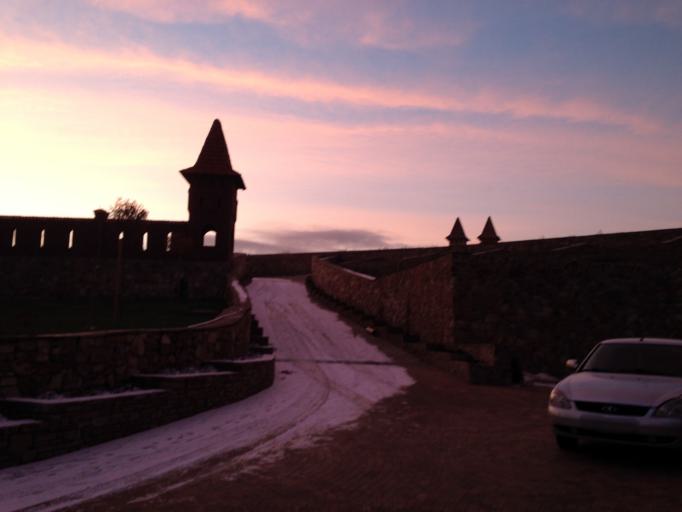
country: RU
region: Rostov
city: Staraya Stanitsa
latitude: 48.3531
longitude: 40.2966
